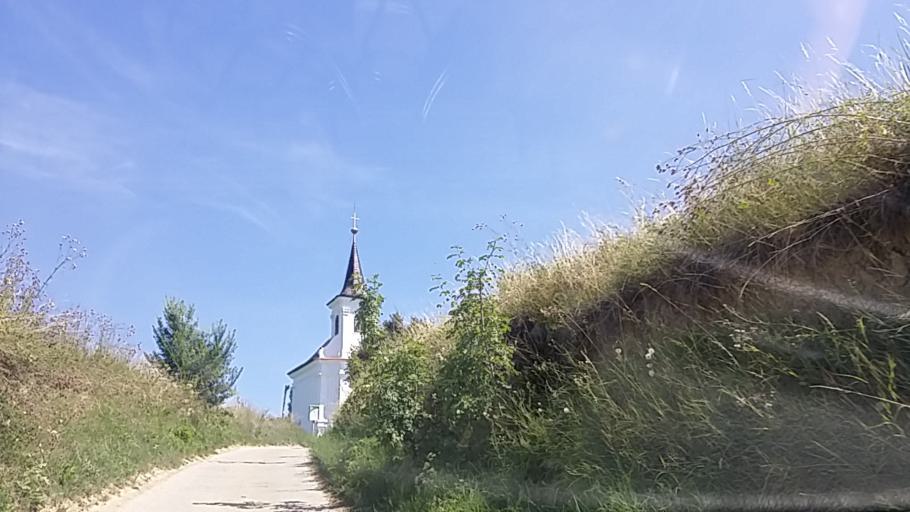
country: HU
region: Somogy
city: Balatonlelle
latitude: 46.7529
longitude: 17.7056
